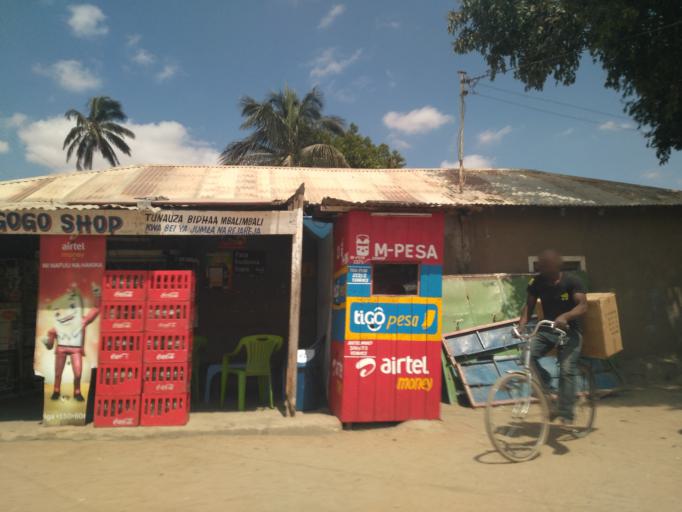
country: TZ
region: Dodoma
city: Dodoma
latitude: -6.1796
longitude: 35.7420
